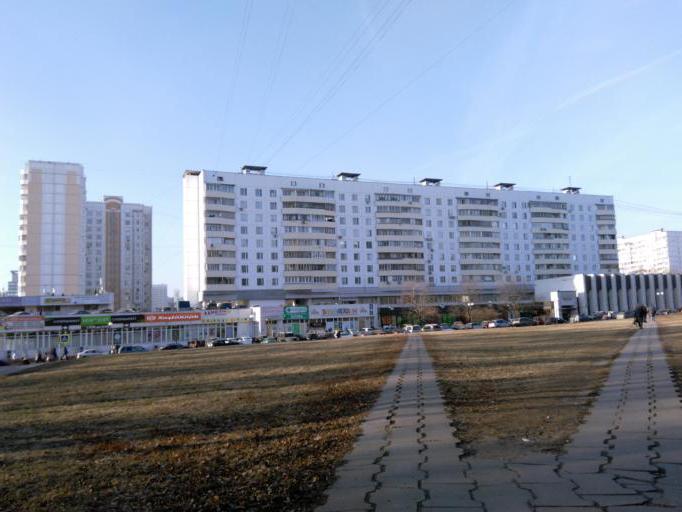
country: RU
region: Moscow
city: Troparevo
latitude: 55.6545
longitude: 37.4863
